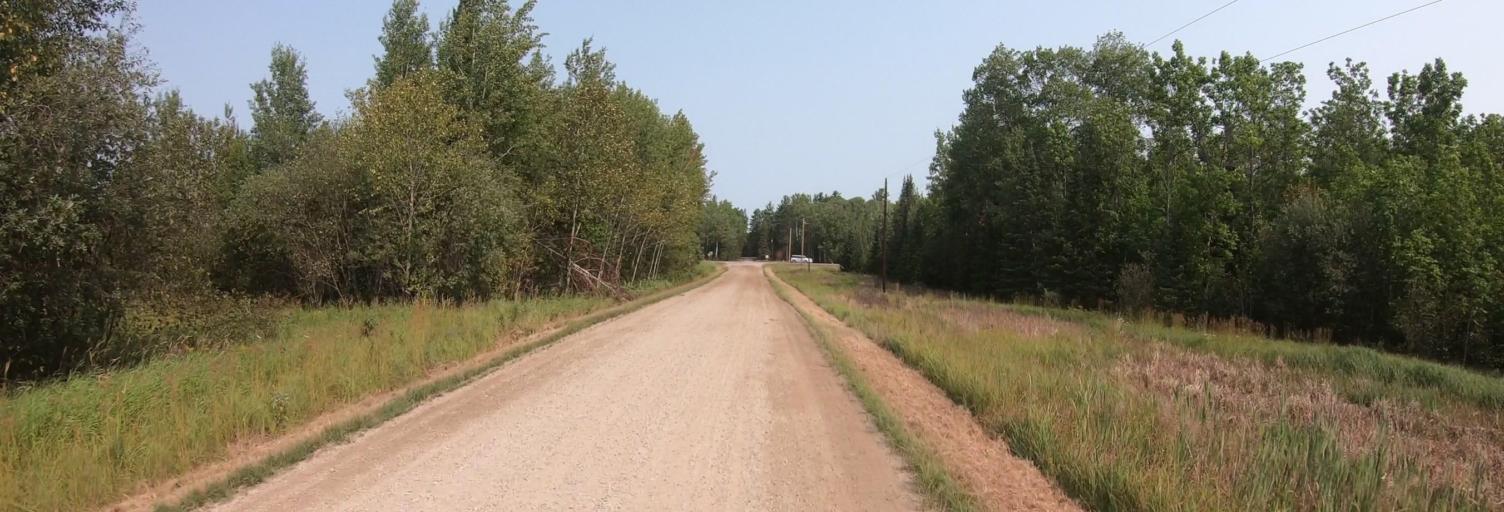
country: US
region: Minnesota
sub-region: Saint Louis County
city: Mountain Iron
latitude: 47.8660
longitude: -92.7399
